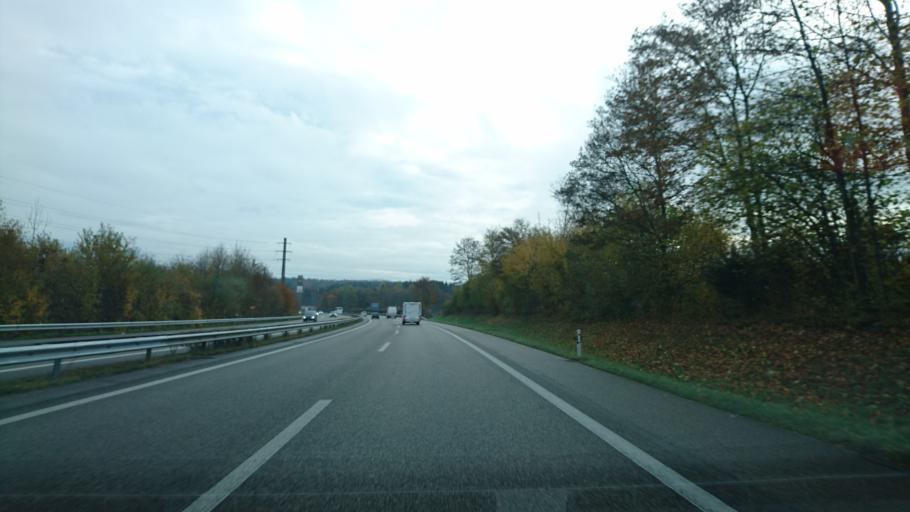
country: CH
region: Aargau
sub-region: Bezirk Zofingen
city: Kolliken
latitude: 47.3217
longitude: 8.0142
